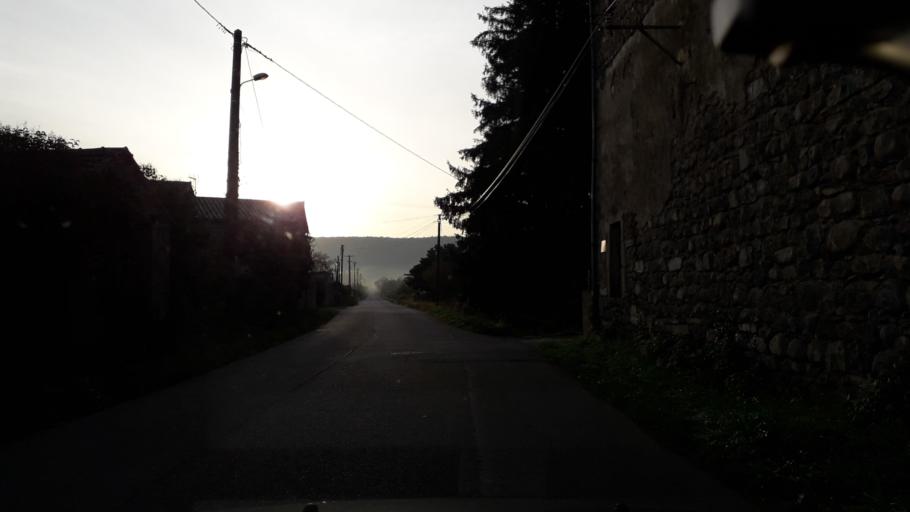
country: FR
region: Rhone-Alpes
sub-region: Departement de l'Ardeche
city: Saint-Privat
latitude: 44.6249
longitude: 4.4217
